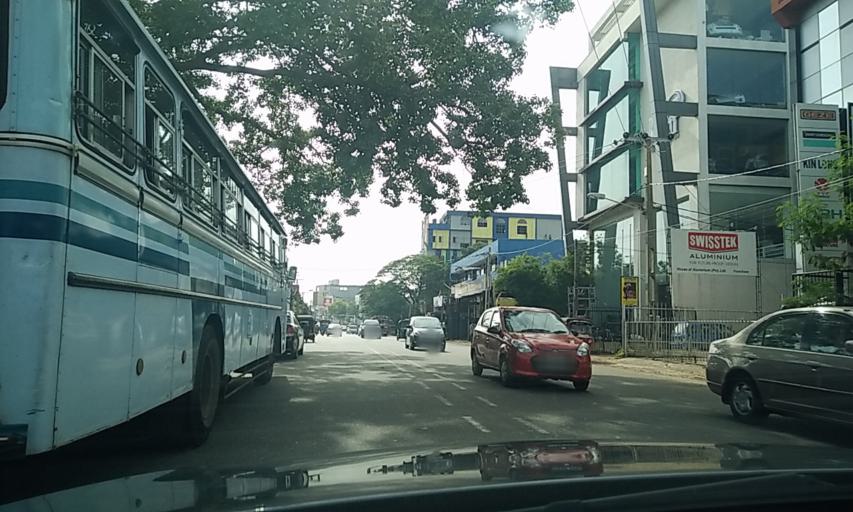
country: LK
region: Western
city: Sri Jayewardenepura Kotte
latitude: 6.8639
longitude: 79.8988
